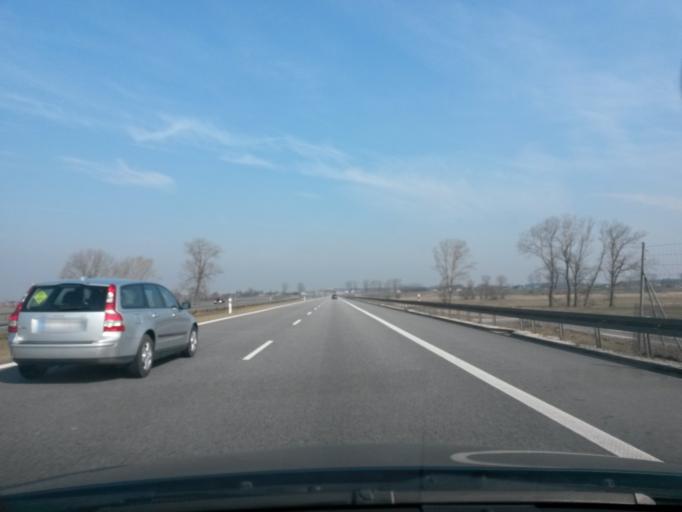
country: PL
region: Lodz Voivodeship
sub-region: Powiat kutnowski
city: Krzyzanow
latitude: 52.1718
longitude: 19.4855
